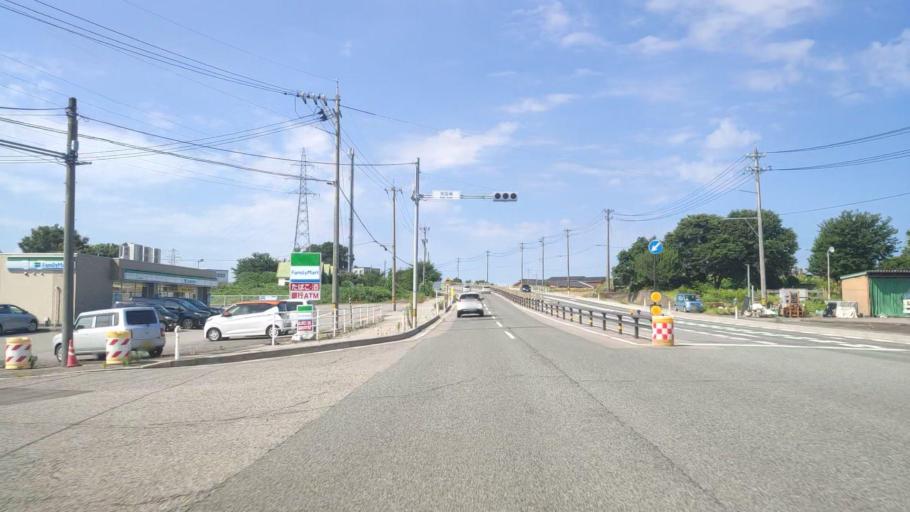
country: JP
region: Ishikawa
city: Komatsu
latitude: 36.4129
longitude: 136.5107
